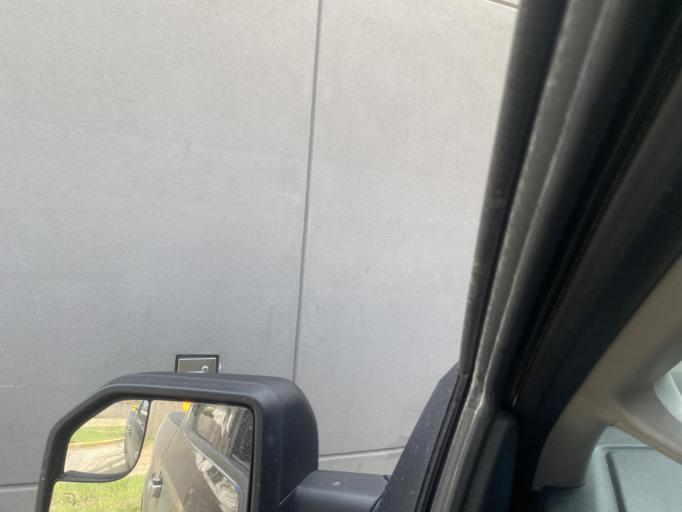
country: CA
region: Manitoba
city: Portage la Prairie
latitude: 49.9724
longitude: -98.3073
